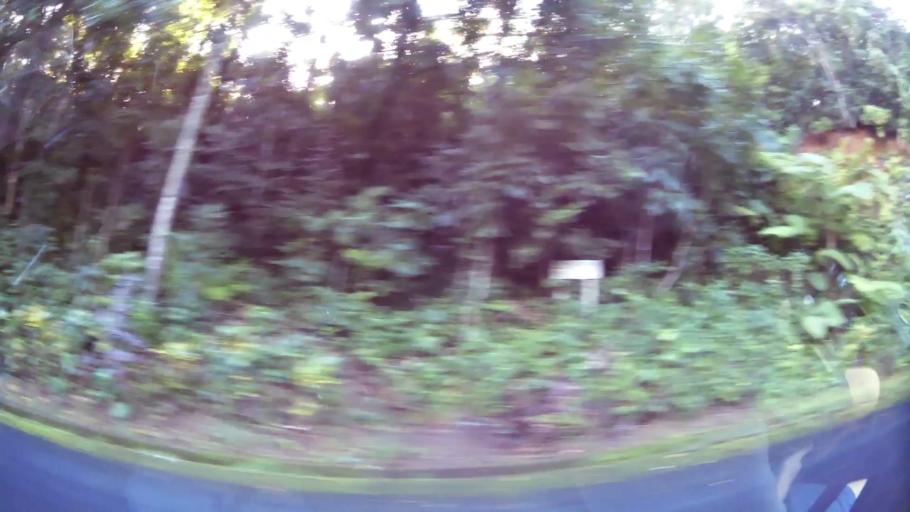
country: DM
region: Saint Andrew
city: Calibishie
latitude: 15.5914
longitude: -61.3556
